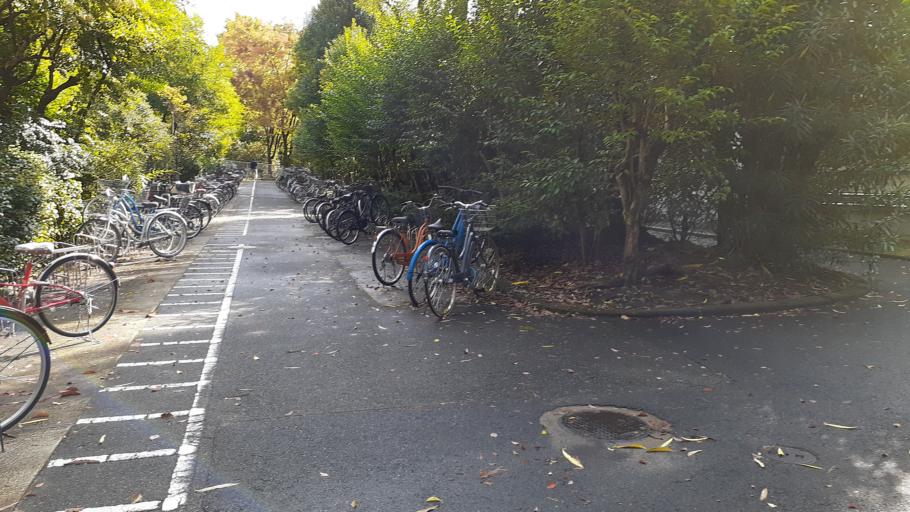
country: JP
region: Kyoto
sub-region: Kyoto-shi
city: Kamigyo-ku
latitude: 35.0301
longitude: 135.7836
